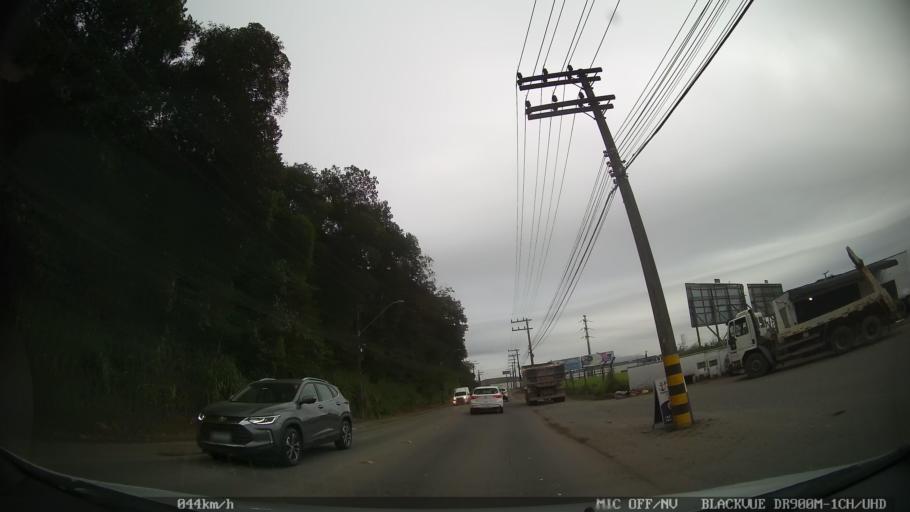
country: BR
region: Santa Catarina
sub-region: Joinville
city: Joinville
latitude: -26.2473
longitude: -48.8808
